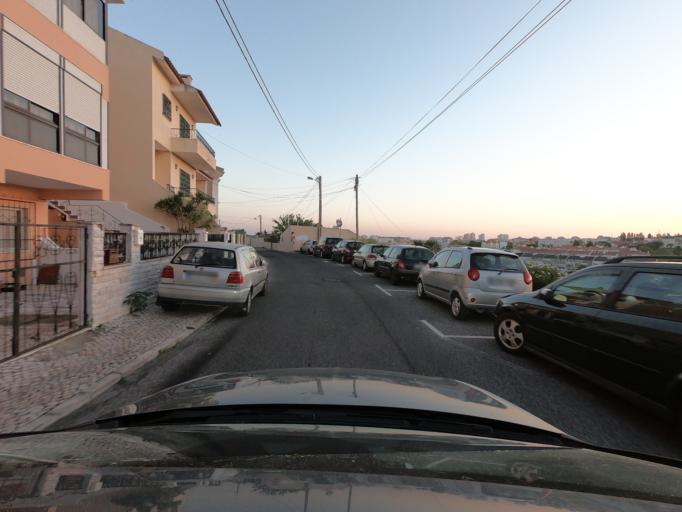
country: PT
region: Lisbon
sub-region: Cascais
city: Sao Domingos de Rana
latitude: 38.7019
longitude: -9.3307
